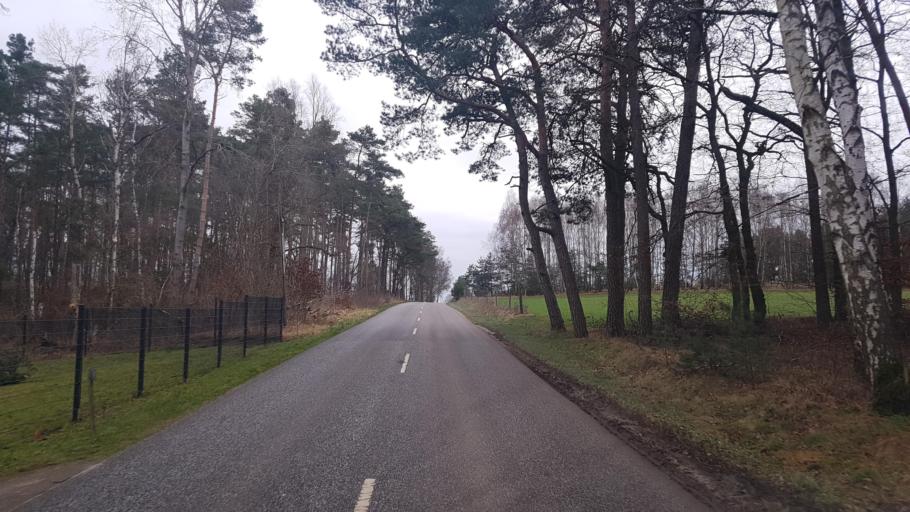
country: DE
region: Brandenburg
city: Oranienburg
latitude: 52.8480
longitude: 13.1557
